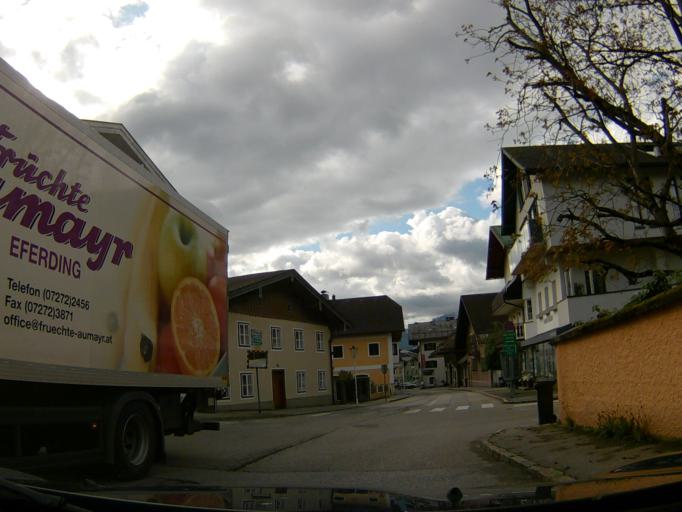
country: AT
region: Upper Austria
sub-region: Politischer Bezirk Vocklabruck
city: Mondsee
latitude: 47.8582
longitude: 13.3473
